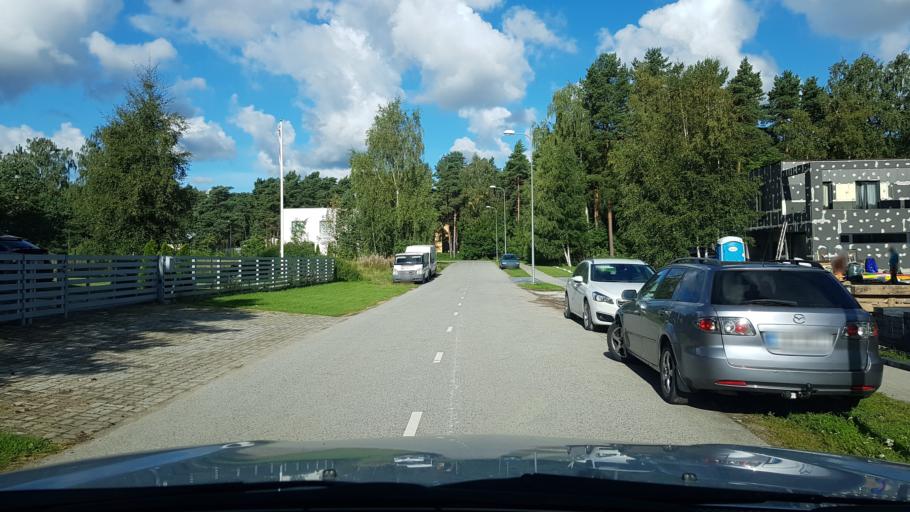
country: EE
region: Harju
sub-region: Tallinna linn
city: Tallinn
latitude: 59.3703
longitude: 24.7663
